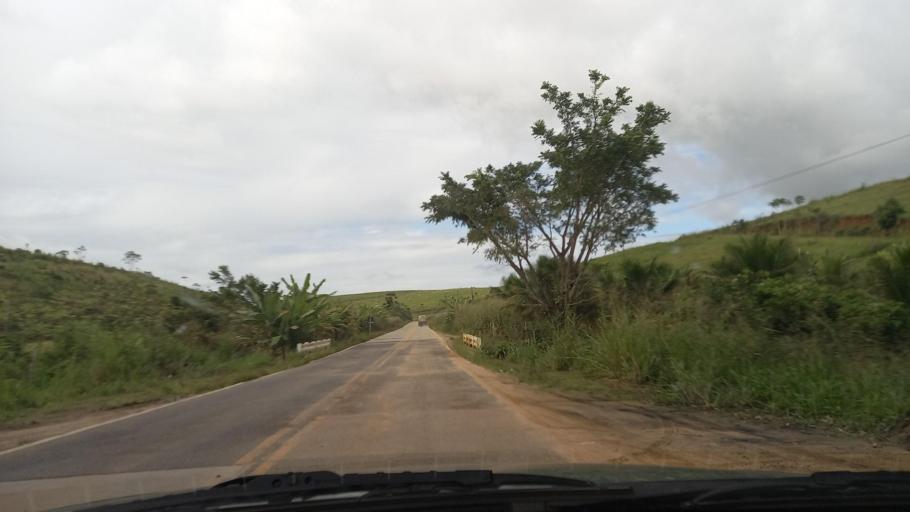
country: BR
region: Pernambuco
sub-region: Maraial
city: Maraial
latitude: -8.7599
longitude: -35.8538
